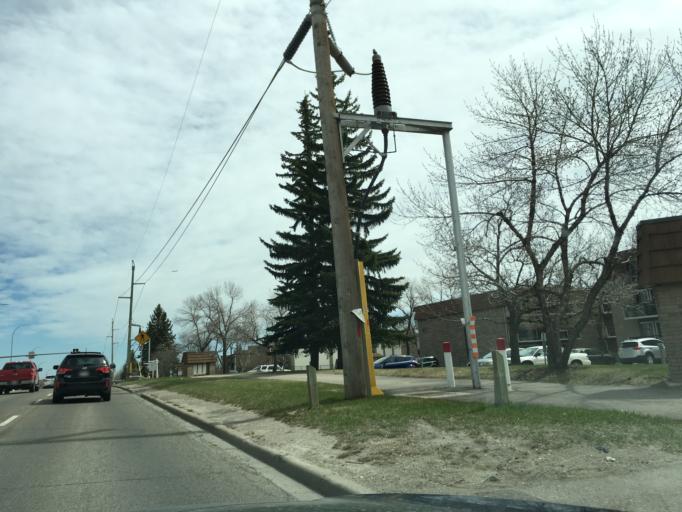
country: CA
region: Alberta
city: Calgary
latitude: 50.9796
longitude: -114.0656
